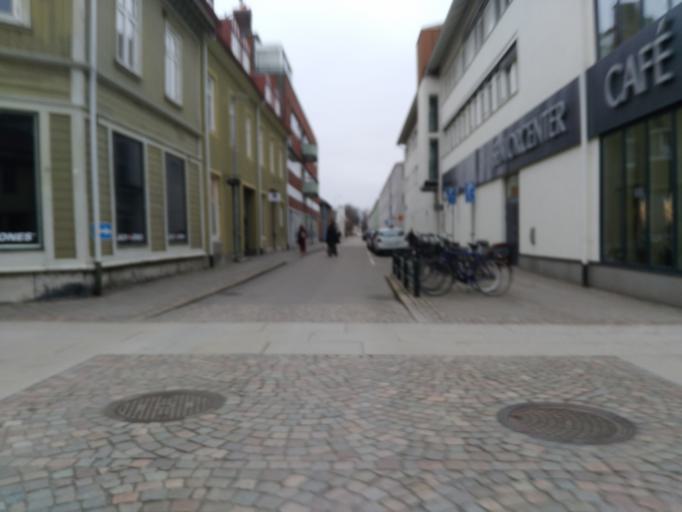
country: SE
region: Vaestra Goetaland
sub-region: Lidkopings Kommun
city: Lidkoping
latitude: 58.5047
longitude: 13.1544
